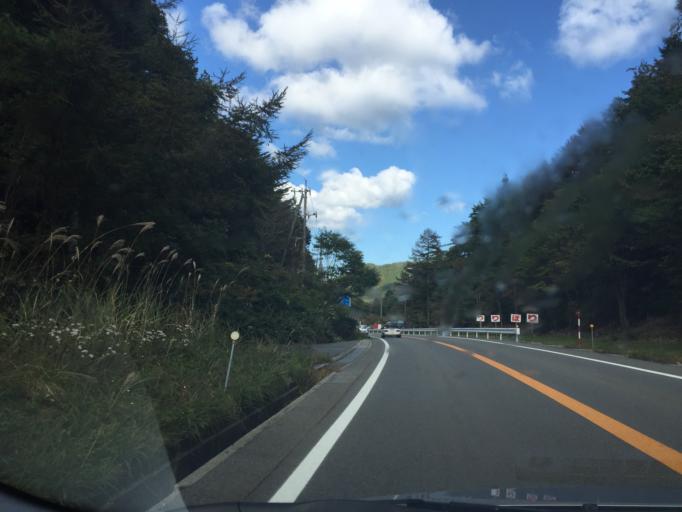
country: JP
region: Gifu
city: Nakatsugawa
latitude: 35.3508
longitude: 137.6673
